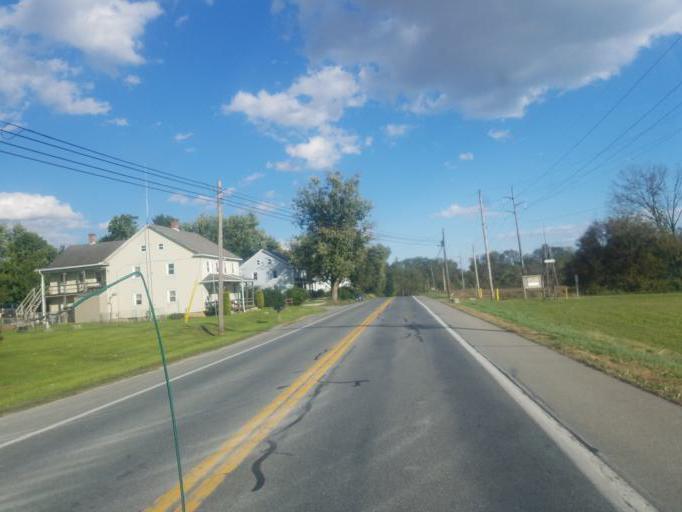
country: US
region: Pennsylvania
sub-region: Lancaster County
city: Bainbridge
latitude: 40.0778
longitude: -76.6504
